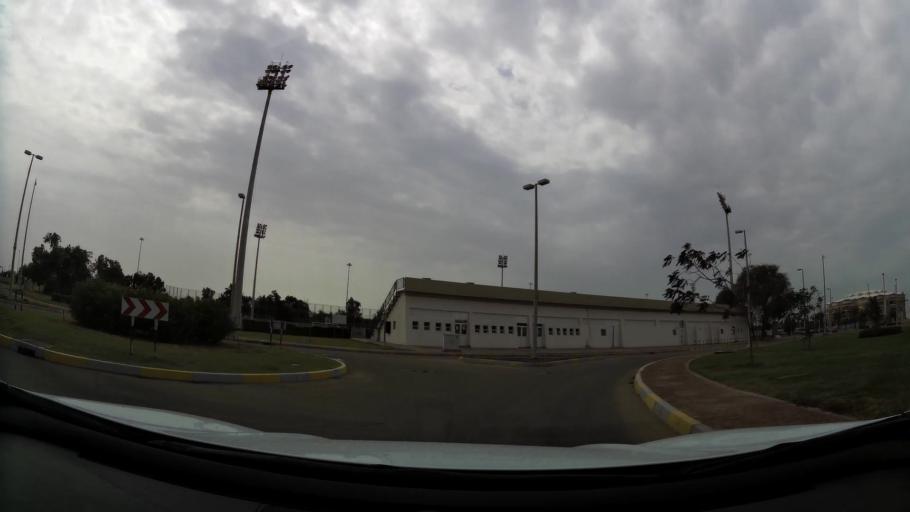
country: AE
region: Abu Dhabi
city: Abu Dhabi
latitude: 24.4125
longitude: 54.4604
